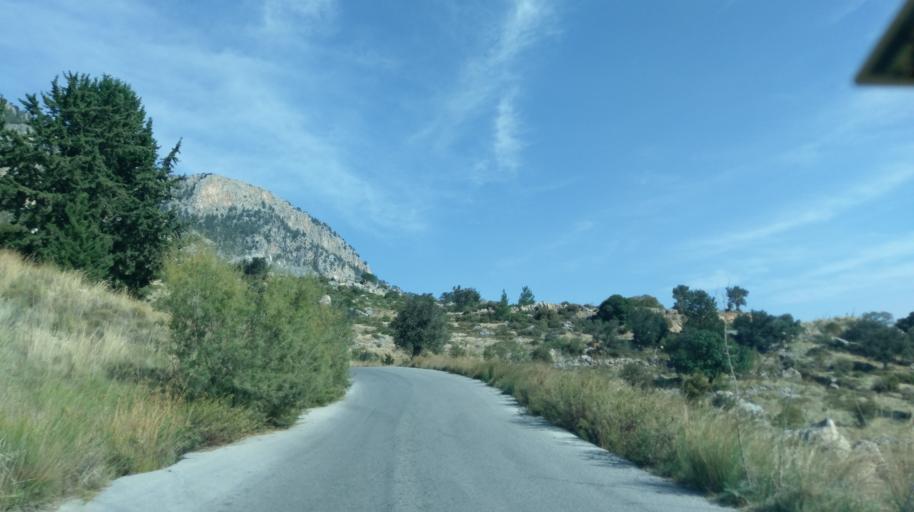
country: CY
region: Keryneia
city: Lapithos
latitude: 35.3041
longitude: 33.1729
